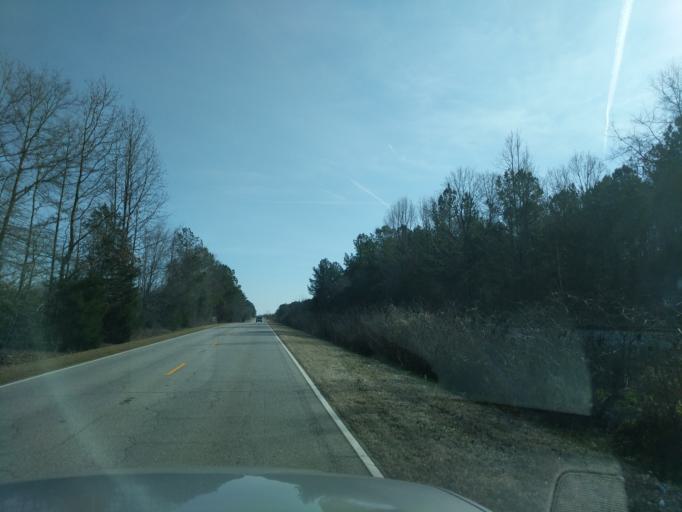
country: US
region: South Carolina
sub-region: Spartanburg County
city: Woodruff
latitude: 34.7119
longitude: -82.0185
